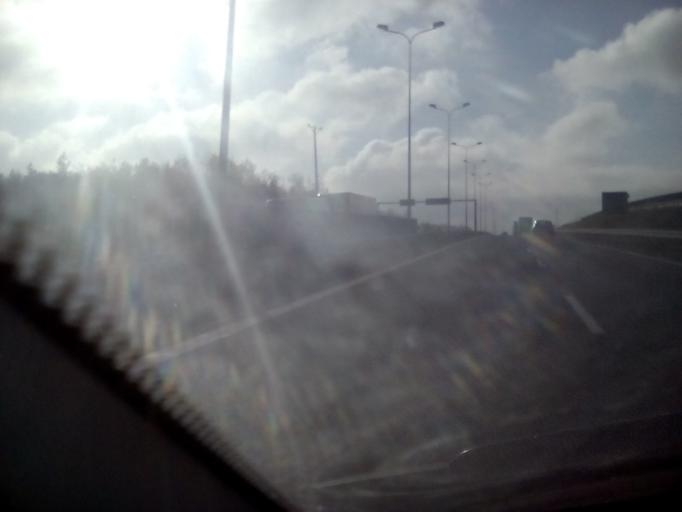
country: PL
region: Masovian Voivodeship
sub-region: Powiat grojecki
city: Goszczyn
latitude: 51.7325
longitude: 20.9160
